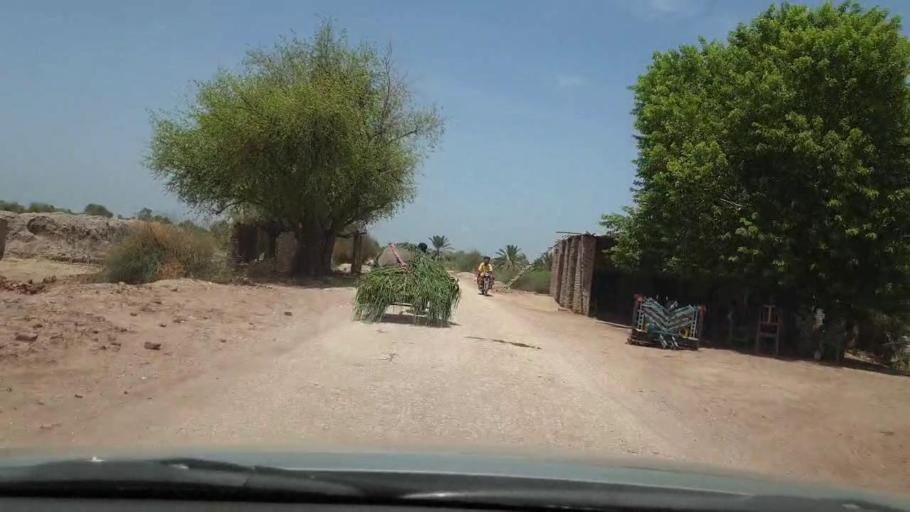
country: PK
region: Sindh
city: Pano Aqil
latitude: 27.7023
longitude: 69.2180
